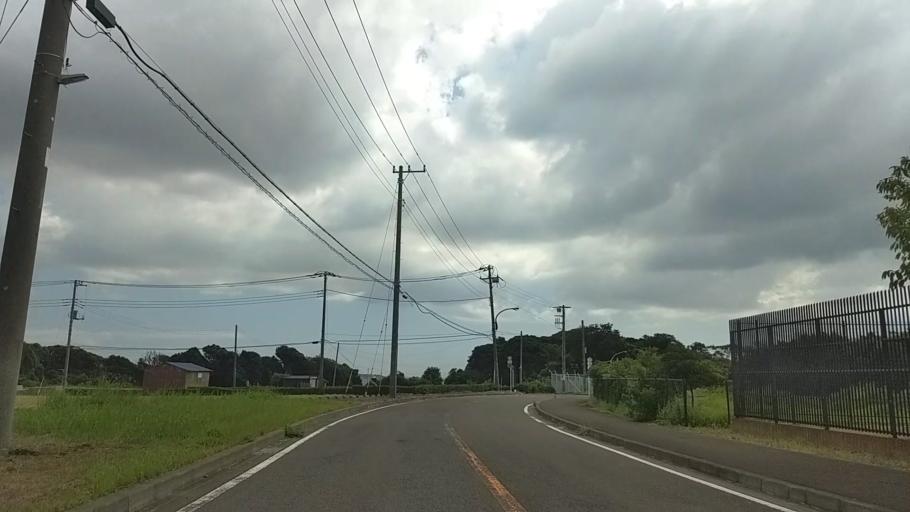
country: JP
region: Kanagawa
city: Miura
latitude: 35.1934
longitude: 139.6145
